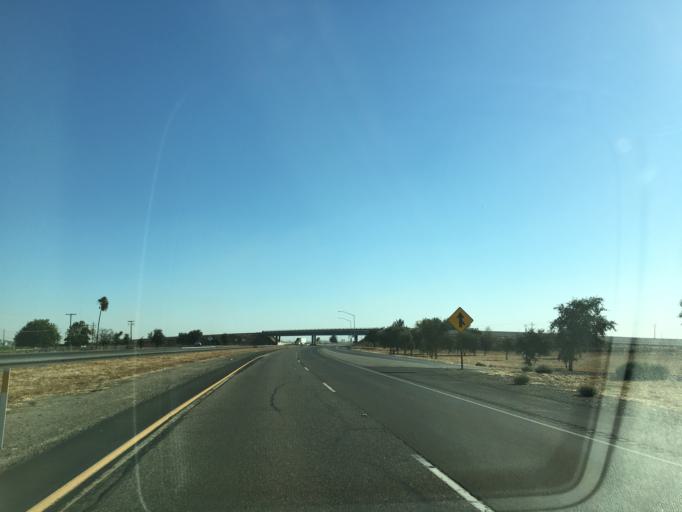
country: US
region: California
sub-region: Merced County
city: Dos Palos
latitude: 37.0821
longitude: -120.4963
